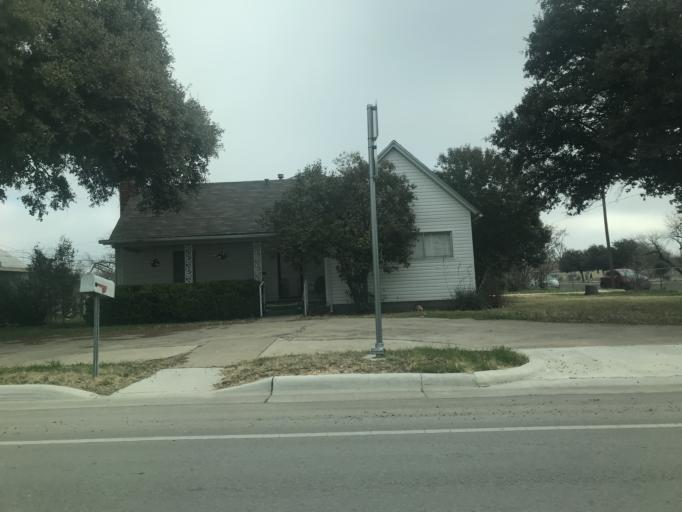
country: US
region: Texas
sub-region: Tom Green County
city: San Angelo
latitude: 31.4760
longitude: -100.4505
